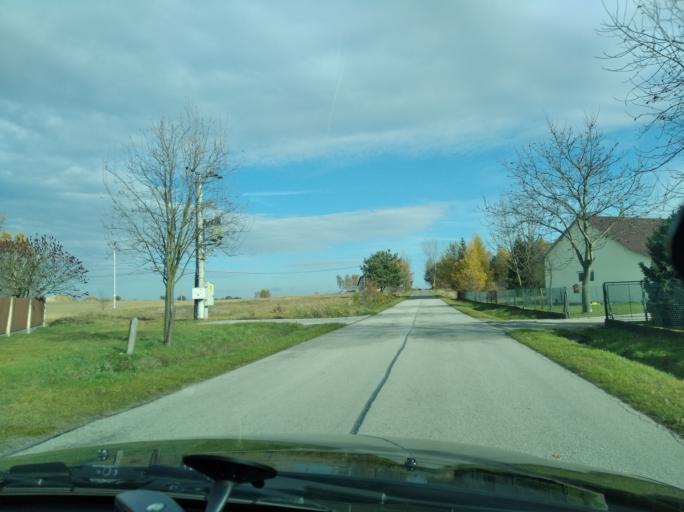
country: PL
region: Subcarpathian Voivodeship
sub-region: Powiat ropczycko-sedziszowski
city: Sedziszow Malopolski
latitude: 50.0998
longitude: 21.6685
